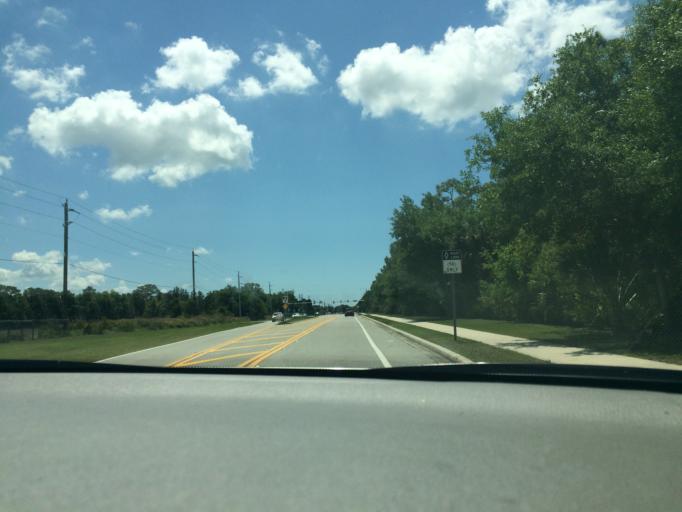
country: US
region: Florida
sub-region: Manatee County
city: Samoset
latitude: 27.4544
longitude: -82.4853
